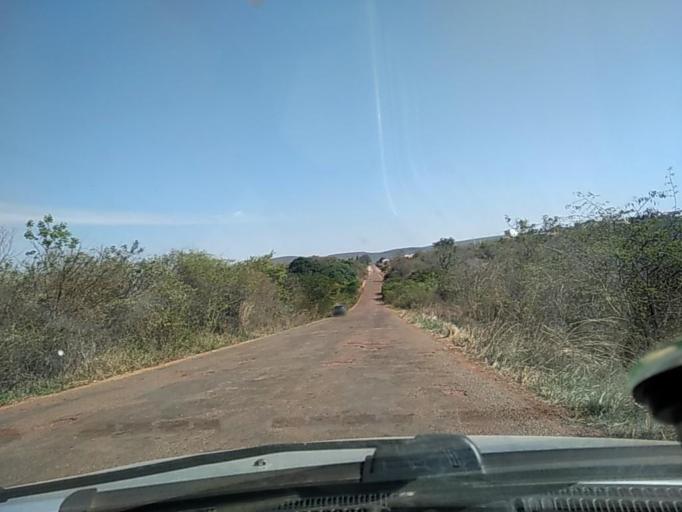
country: BR
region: Bahia
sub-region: Caetite
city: Caetite
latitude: -14.0435
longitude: -42.4858
